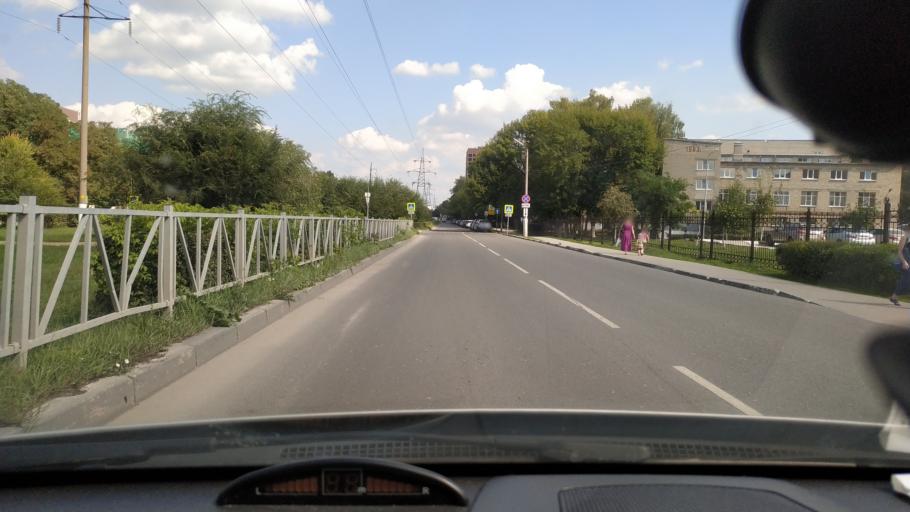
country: RU
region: Rjazan
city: Ryazan'
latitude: 54.6229
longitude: 39.7108
